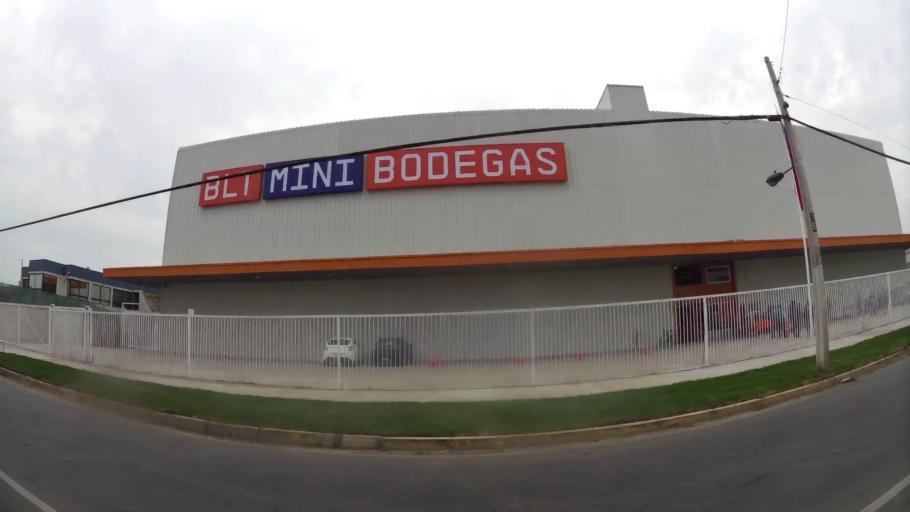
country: CL
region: Santiago Metropolitan
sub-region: Provincia de Santiago
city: Villa Presidente Frei, Nunoa, Santiago, Chile
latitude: -33.4800
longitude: -70.6061
